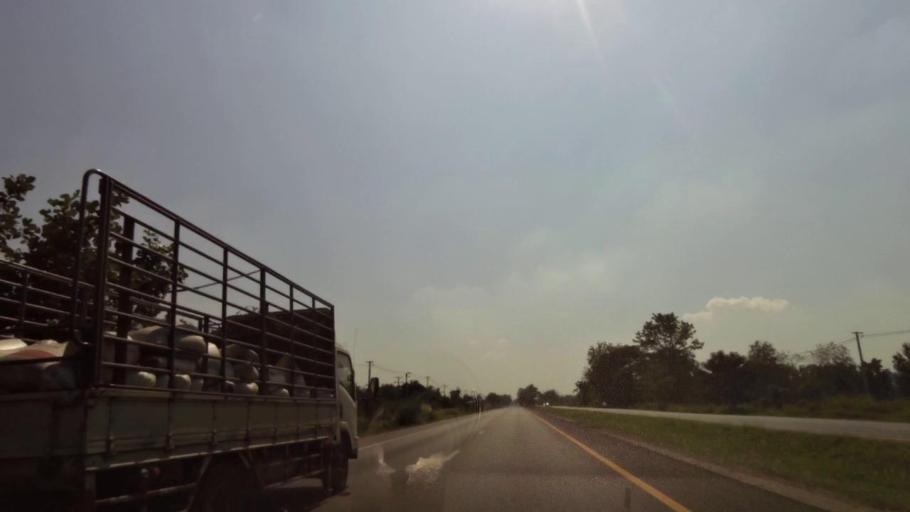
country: TH
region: Phichit
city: Bueng Na Rang
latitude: 16.2607
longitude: 100.1260
